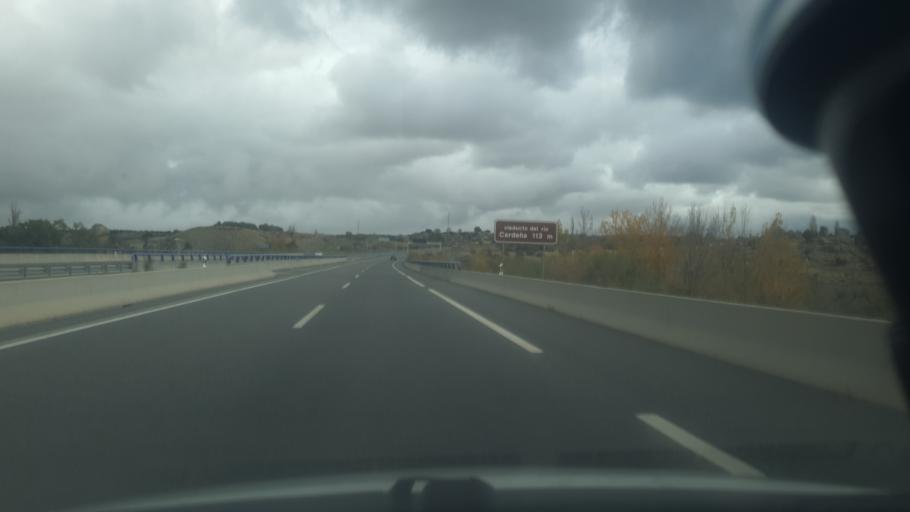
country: ES
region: Castille and Leon
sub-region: Provincia de Segovia
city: Villacastin
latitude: 40.7627
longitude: -4.4405
